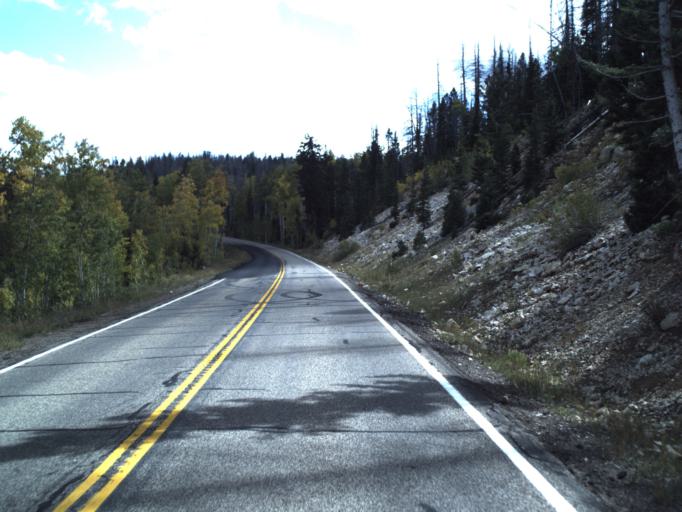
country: US
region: Utah
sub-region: Iron County
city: Parowan
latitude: 37.5363
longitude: -112.7738
